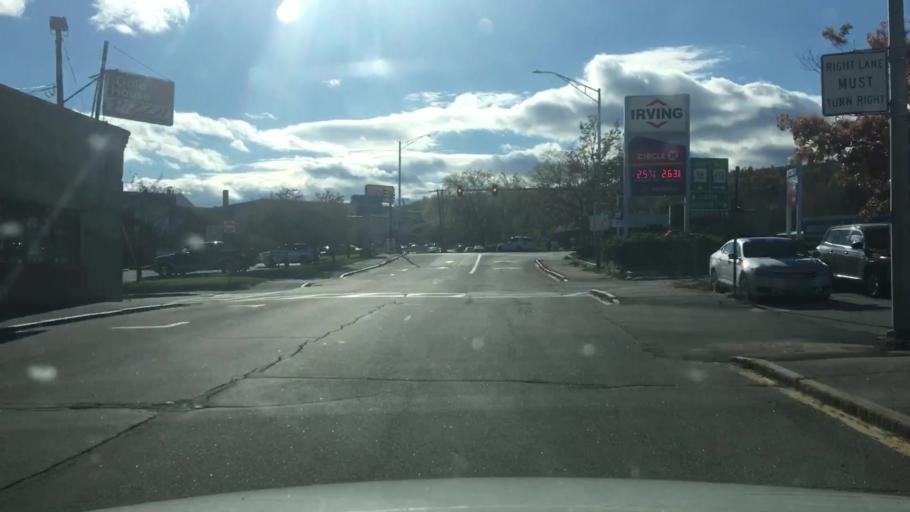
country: US
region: New Hampshire
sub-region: Coos County
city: Berlin
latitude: 44.4692
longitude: -71.1830
